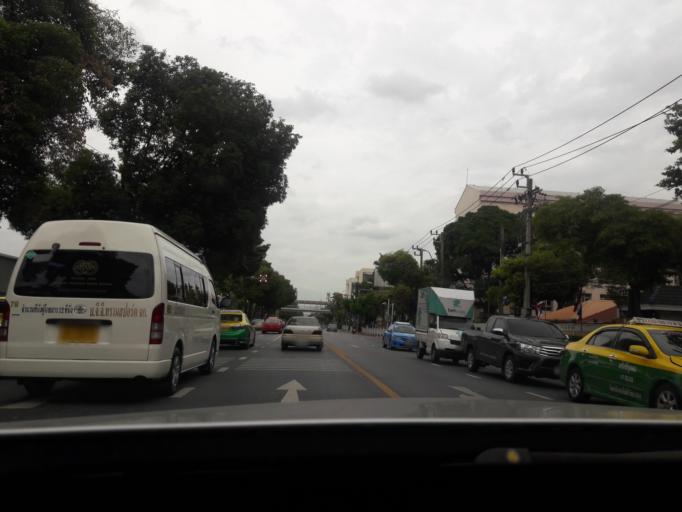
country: TH
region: Bangkok
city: Dusit
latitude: 13.7786
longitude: 100.5160
